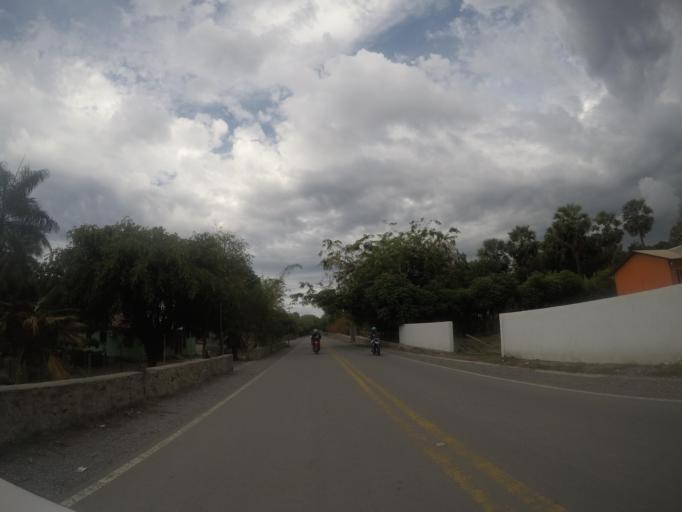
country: TL
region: Liquica
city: Liquica
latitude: -8.5915
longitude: 125.3293
